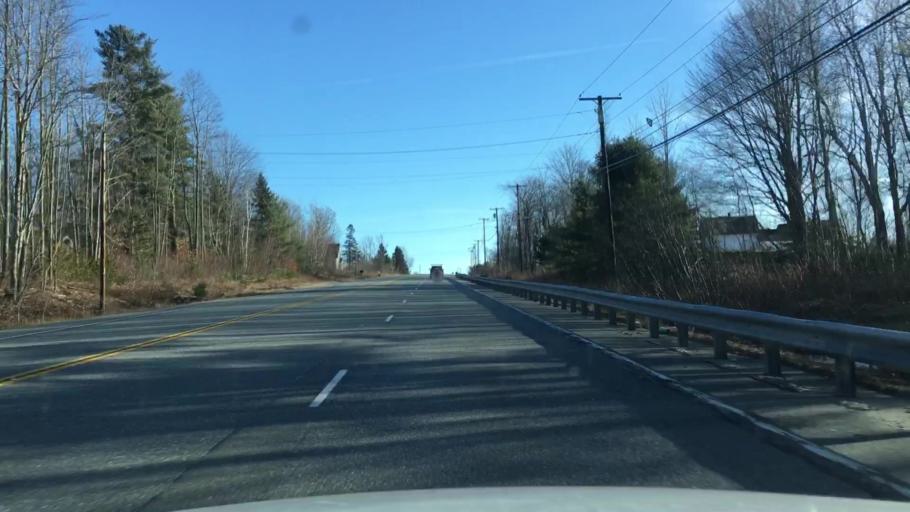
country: US
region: Maine
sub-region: Hancock County
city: Dedham
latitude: 44.6291
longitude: -68.5391
